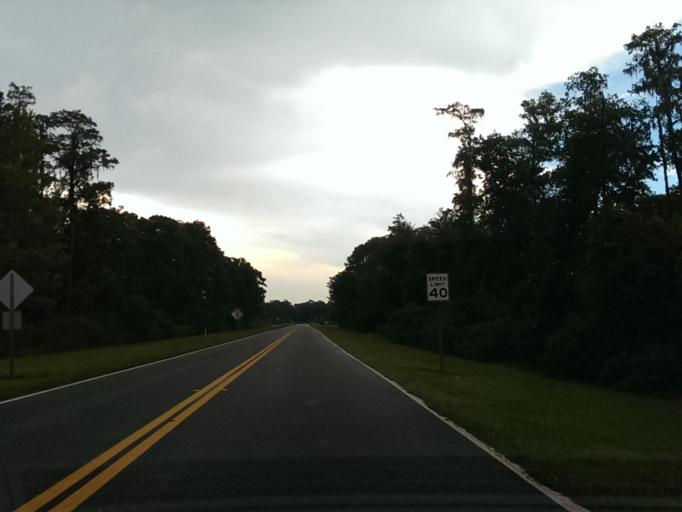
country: US
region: Florida
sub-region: Orange County
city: Bay Hill
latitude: 28.4192
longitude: -81.5888
